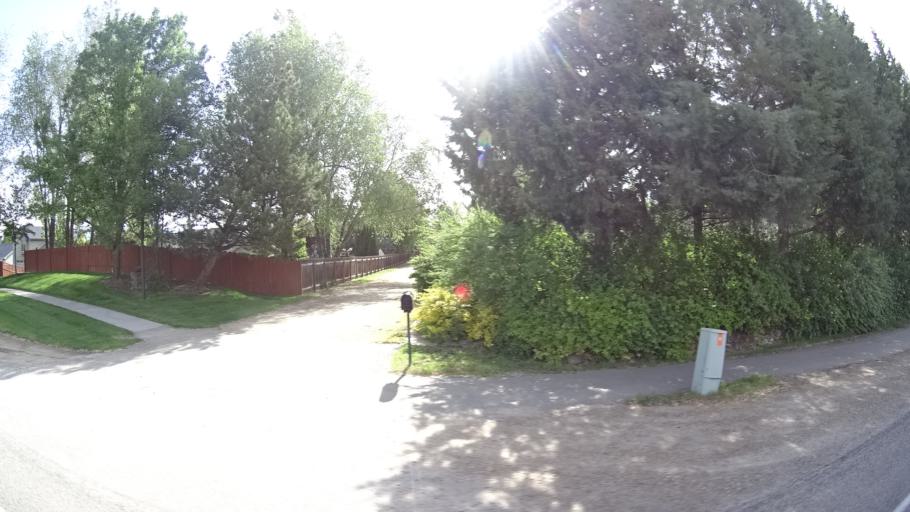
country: US
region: Idaho
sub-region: Ada County
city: Meridian
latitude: 43.5574
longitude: -116.3343
